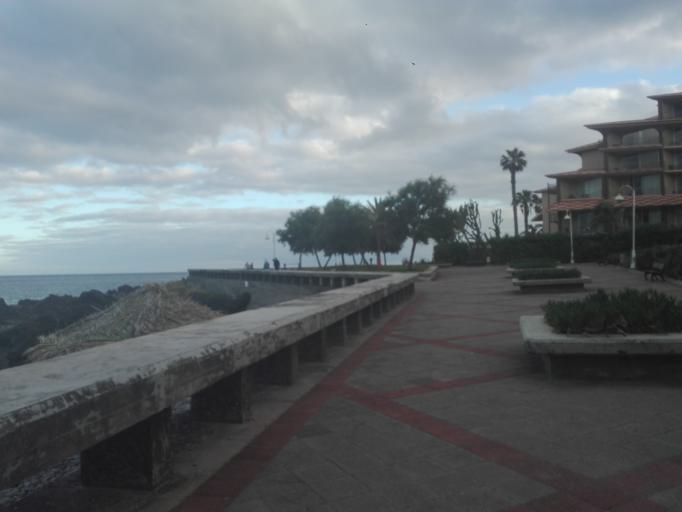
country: PT
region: Madeira
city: Canico
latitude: 32.6467
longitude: -16.8246
